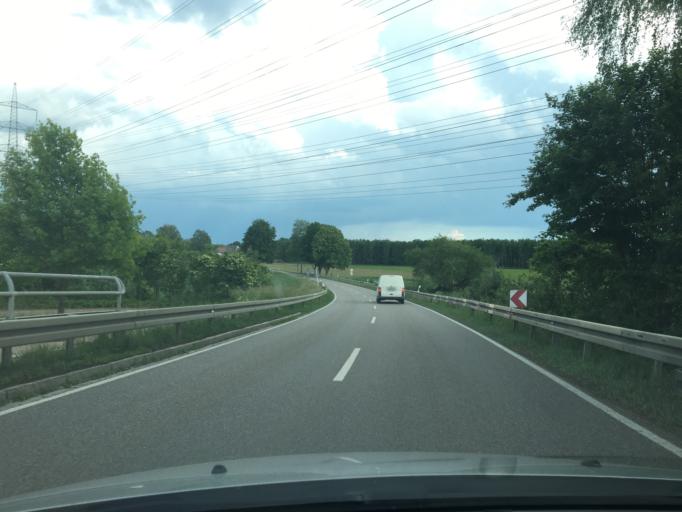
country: DE
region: Bavaria
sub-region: Upper Bavaria
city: Hebertshausen
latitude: 48.3190
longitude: 11.4845
